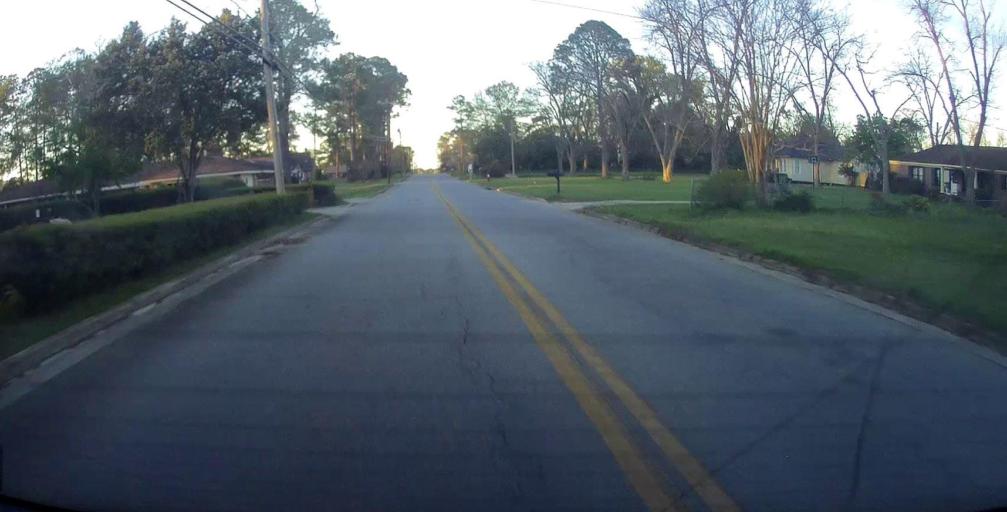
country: US
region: Georgia
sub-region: Crisp County
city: Cordele
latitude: 31.9577
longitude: -83.7655
